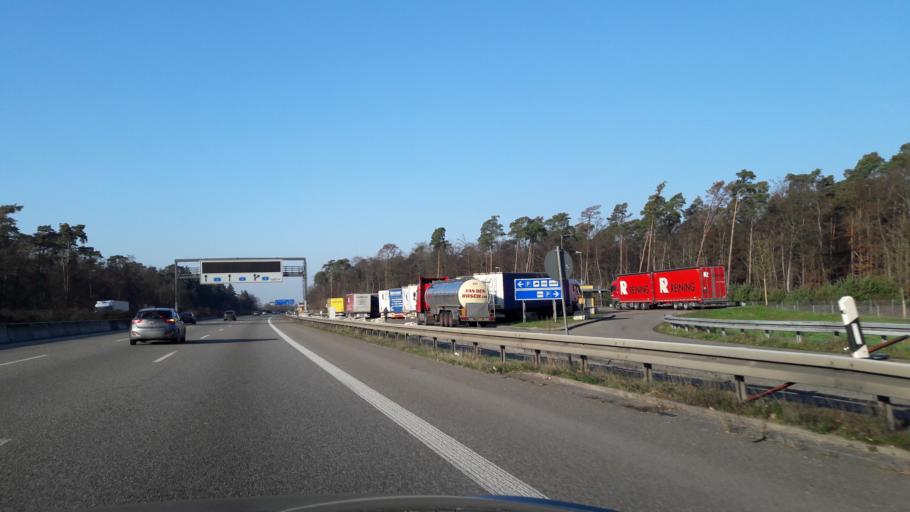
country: DE
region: Baden-Wuerttemberg
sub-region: Karlsruhe Region
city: Sankt Leon-Rot
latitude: 49.2732
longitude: 8.6469
